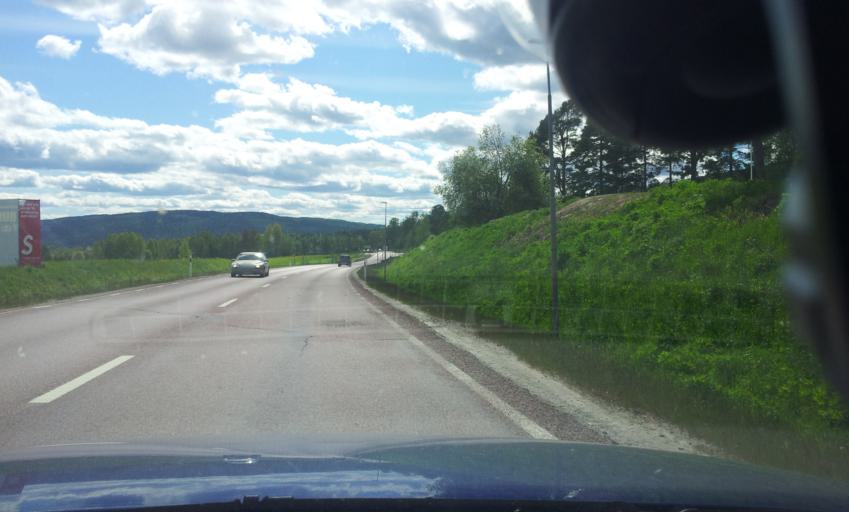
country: SE
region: Gaevleborg
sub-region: Ljusdals Kommun
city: Jaervsoe
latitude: 61.6980
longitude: 16.1614
